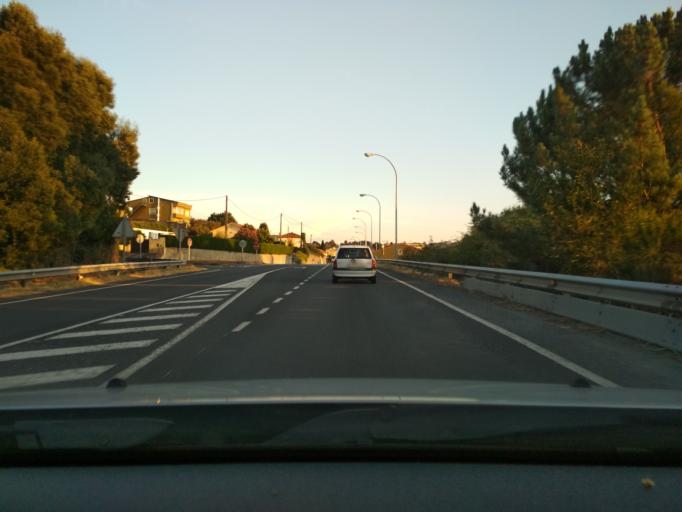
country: ES
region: Galicia
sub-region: Provincia da Coruna
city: Culleredo
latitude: 43.2833
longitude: -8.3674
